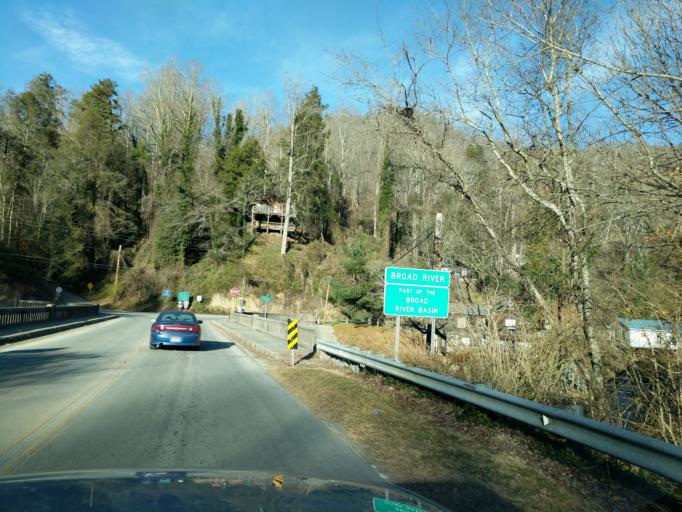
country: US
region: North Carolina
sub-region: Henderson County
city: Edneyville
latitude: 35.4509
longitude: -82.2873
